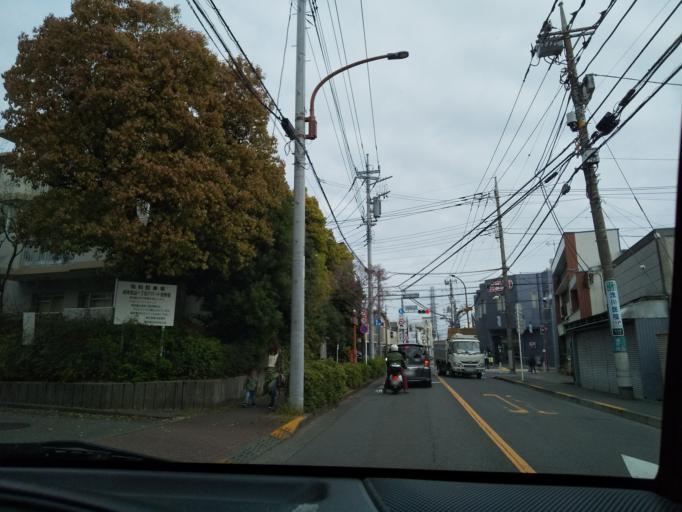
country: JP
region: Tokyo
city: Kokubunji
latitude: 35.6859
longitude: 139.4561
